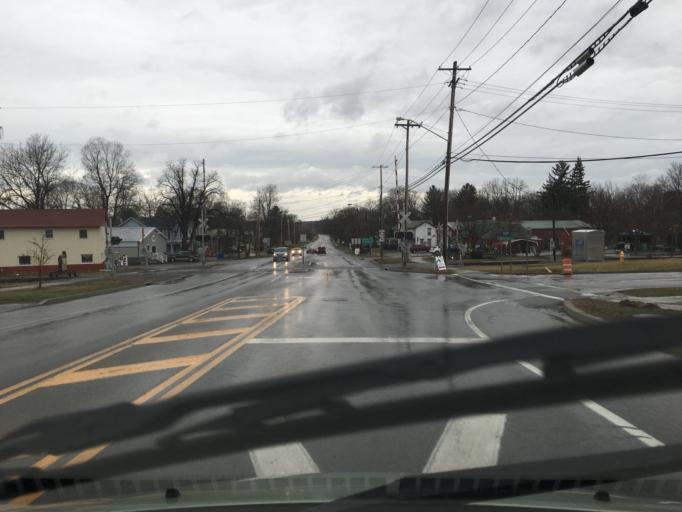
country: US
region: New York
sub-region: Livingston County
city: Avon
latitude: 42.9130
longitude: -77.7477
